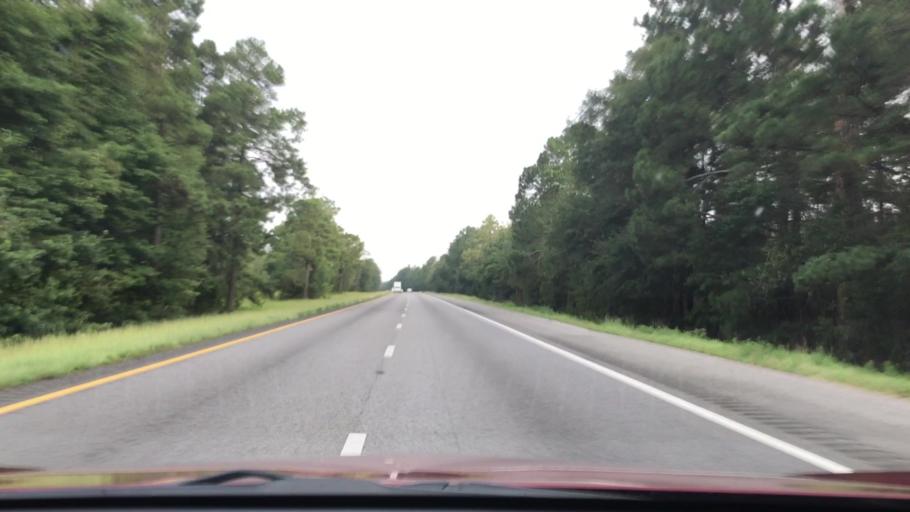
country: US
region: South Carolina
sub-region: Dorchester County
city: Ridgeville
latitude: 33.1695
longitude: -80.3636
